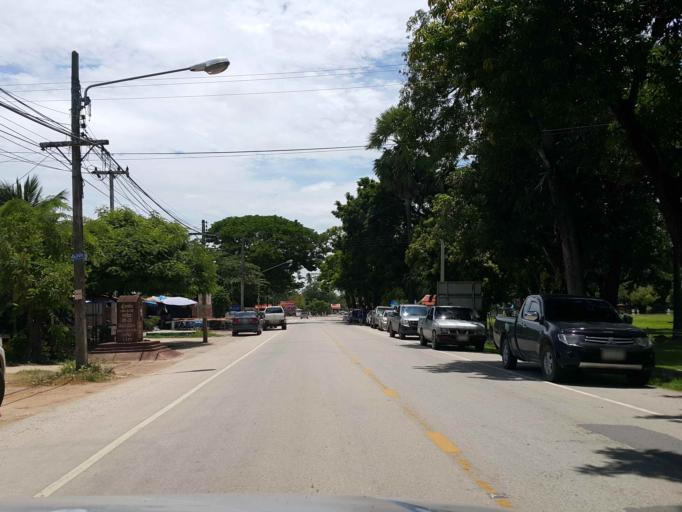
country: TH
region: Sukhothai
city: Ban Na
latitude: 17.0205
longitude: 99.7067
